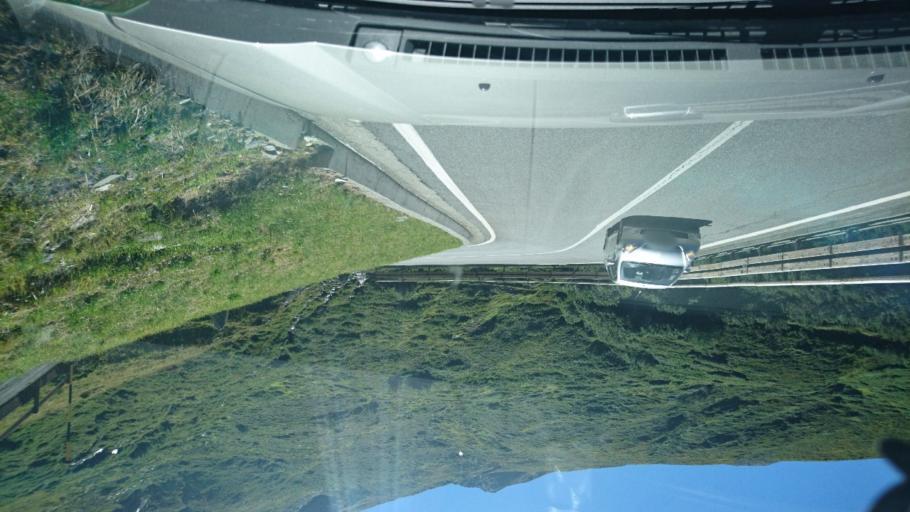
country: IT
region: Aosta Valley
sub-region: Valle d'Aosta
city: San Leonardo
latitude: 45.8556
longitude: 7.1447
